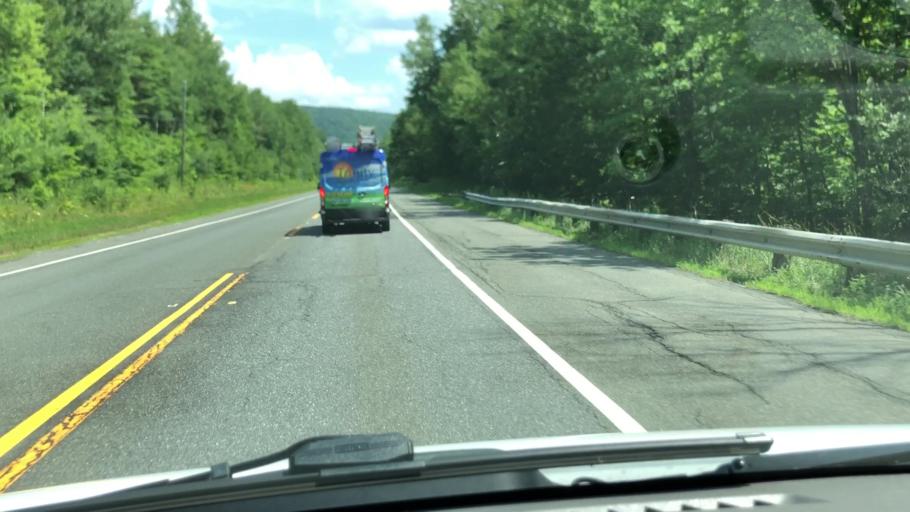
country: US
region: Massachusetts
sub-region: Berkshire County
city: Hinsdale
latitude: 42.4907
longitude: -72.9969
